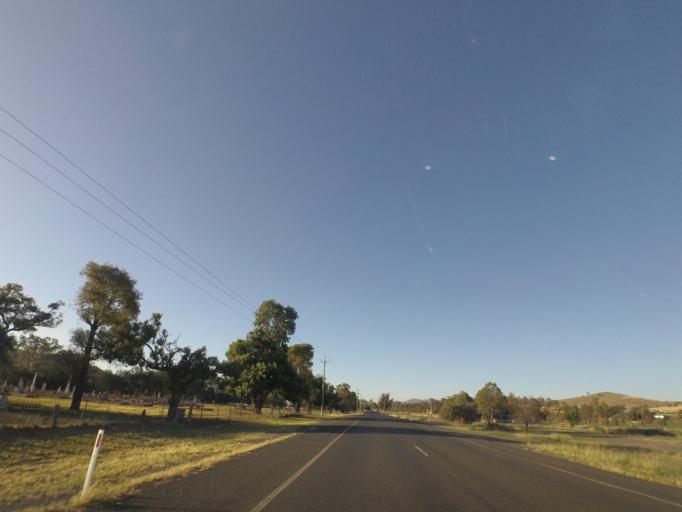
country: AU
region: New South Wales
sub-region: Gundagai
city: Gundagai
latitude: -34.9328
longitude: 148.1669
